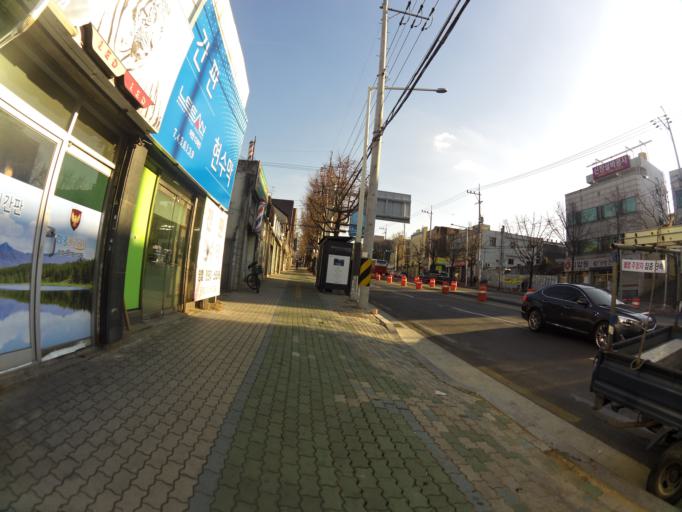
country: KR
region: Daegu
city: Daegu
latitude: 35.8769
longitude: 128.6329
